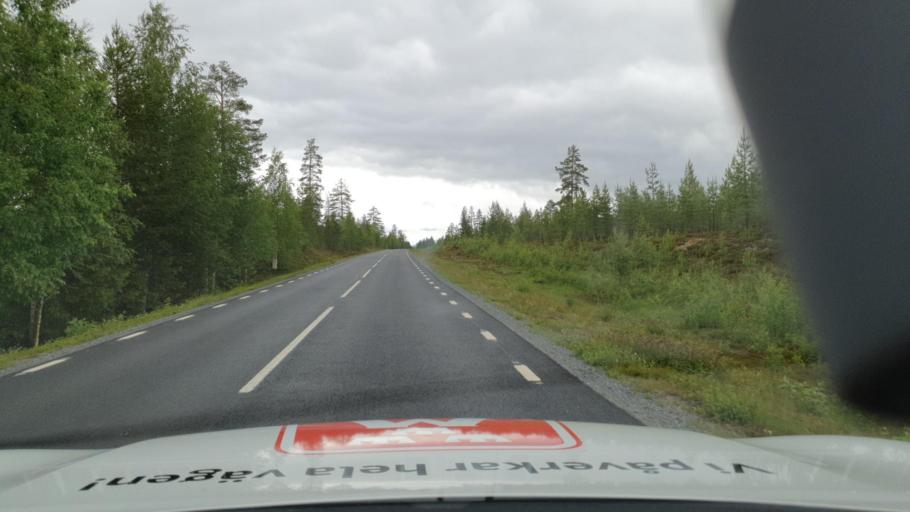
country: SE
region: Vaesterbotten
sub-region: Dorotea Kommun
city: Dorotea
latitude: 64.2069
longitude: 16.5607
